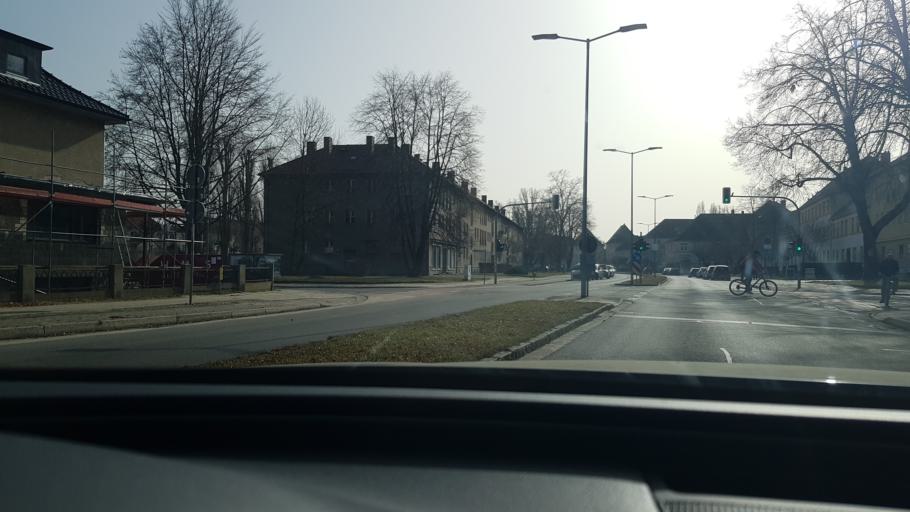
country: DE
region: Brandenburg
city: Guben
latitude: 51.9451
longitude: 14.7040
